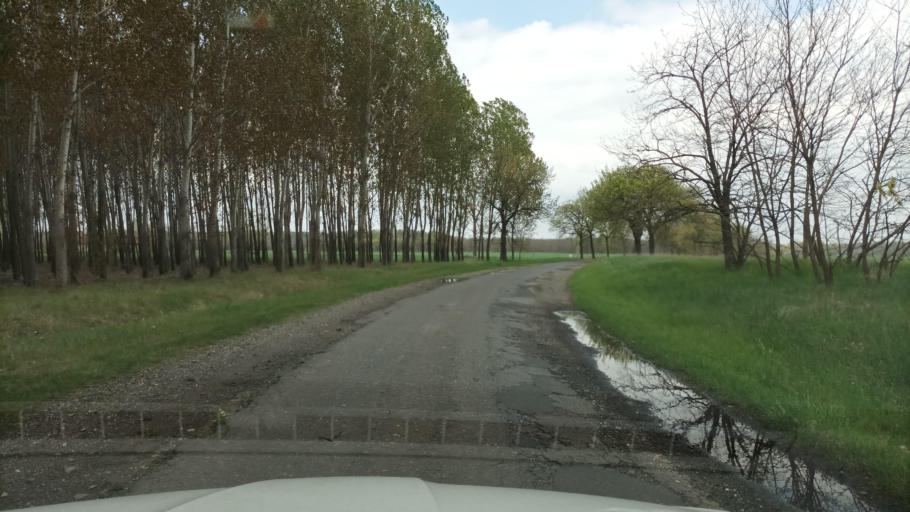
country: HU
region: Pest
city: Kocser
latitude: 47.0528
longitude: 19.8757
